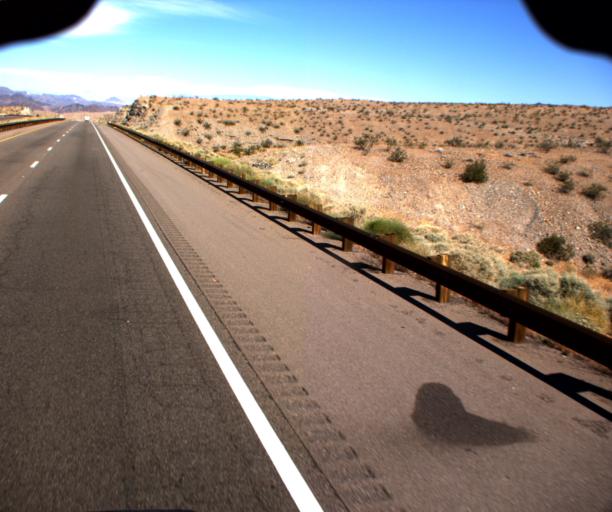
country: US
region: Nevada
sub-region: Clark County
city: Boulder City
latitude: 35.9578
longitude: -114.6589
